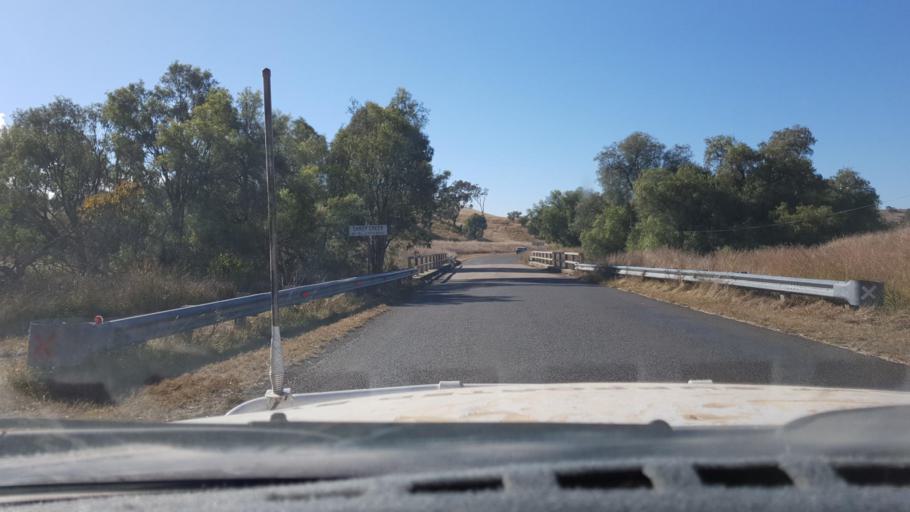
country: AU
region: New South Wales
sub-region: Narrabri
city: Blair Athol
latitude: -30.6716
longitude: 150.3865
